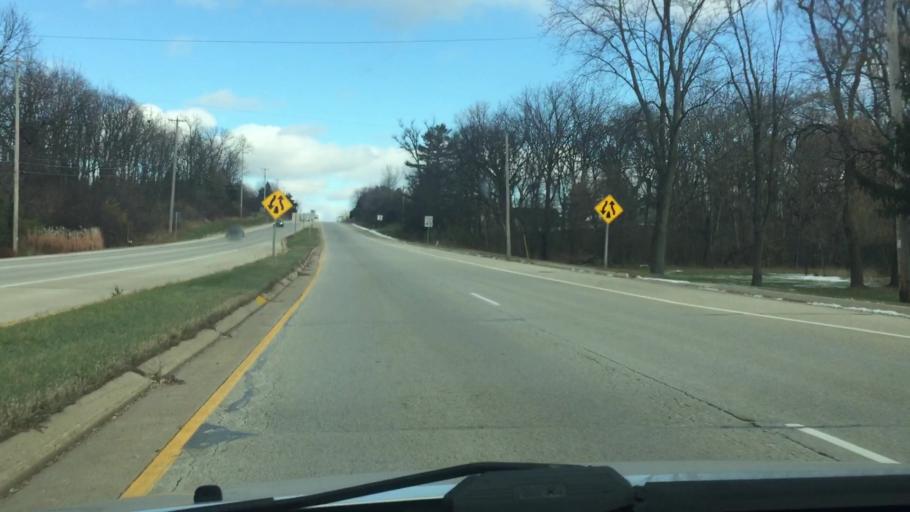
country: US
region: Wisconsin
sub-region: Waukesha County
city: Delafield
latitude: 43.0646
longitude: -88.3674
